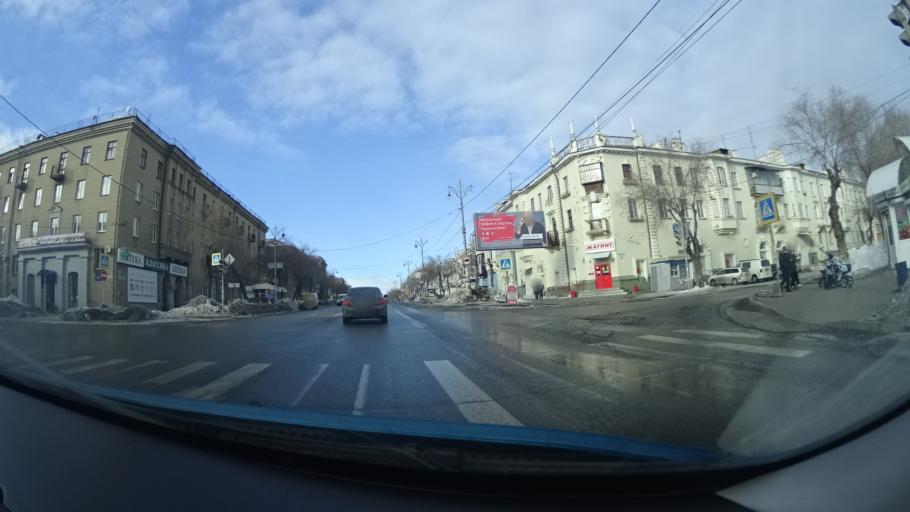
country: RU
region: Chelyabinsk
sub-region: Gorod Magnitogorsk
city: Magnitogorsk
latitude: 53.4280
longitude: 58.9836
